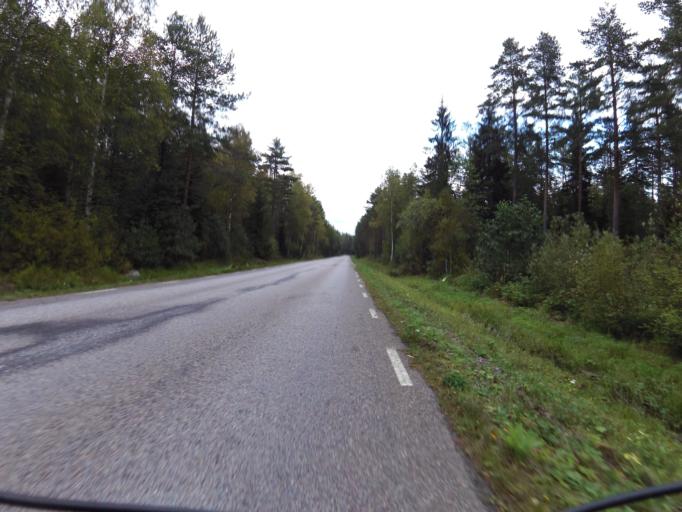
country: SE
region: Gaevleborg
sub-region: Sandvikens Kommun
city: Sandviken
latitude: 60.6557
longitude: 16.8388
